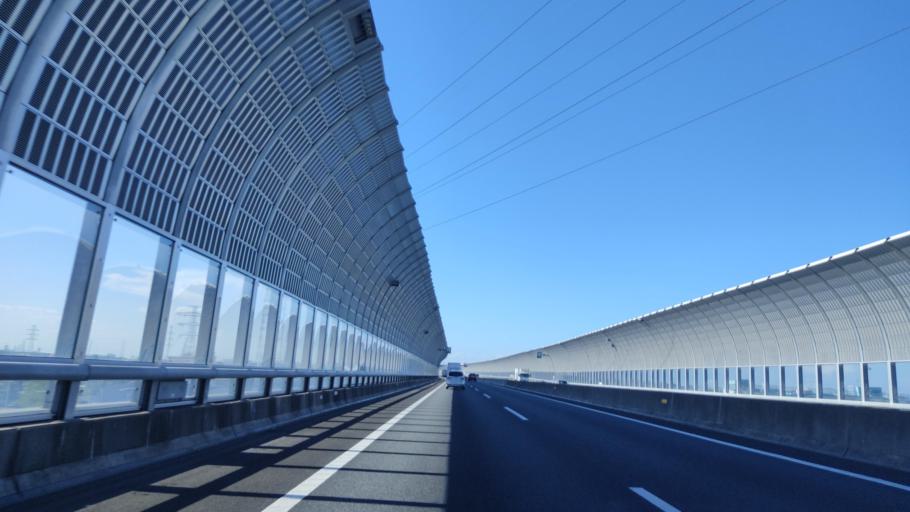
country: JP
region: Chiba
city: Matsudo
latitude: 35.8000
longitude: 139.8764
